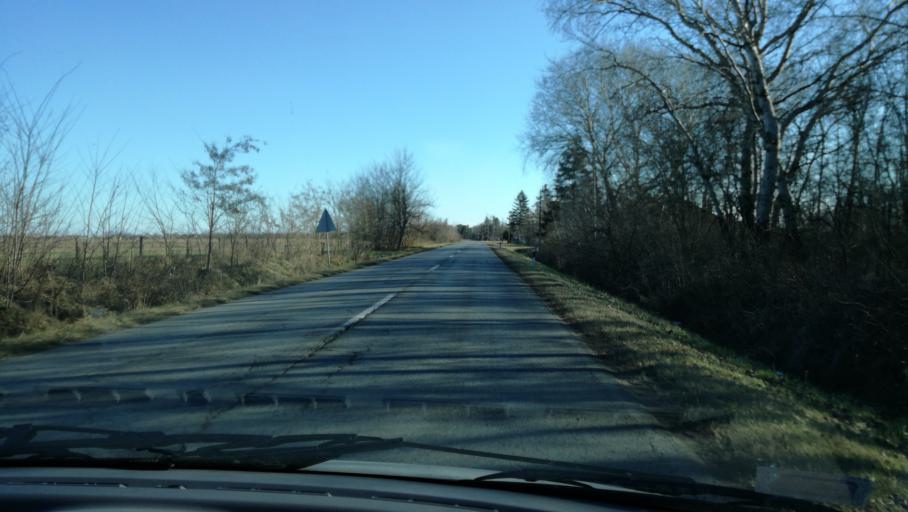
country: HU
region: Csongrad
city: Asotthalom
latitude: 46.1059
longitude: 19.8493
